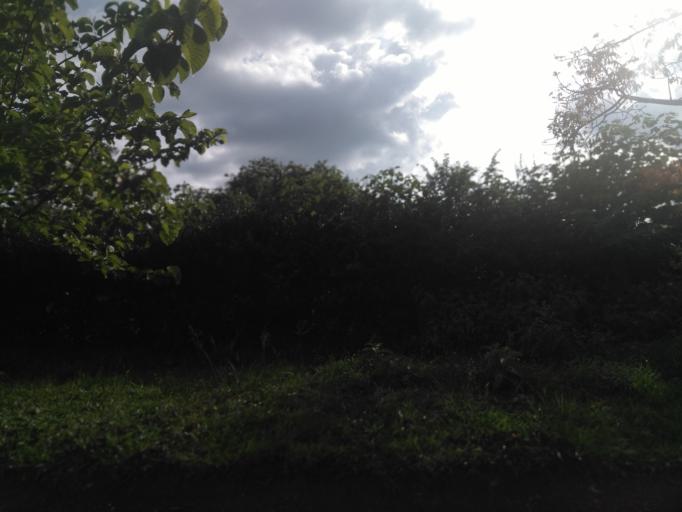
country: UG
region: Eastern Region
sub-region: Jinja District
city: Jinja
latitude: 0.4243
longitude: 33.2026
